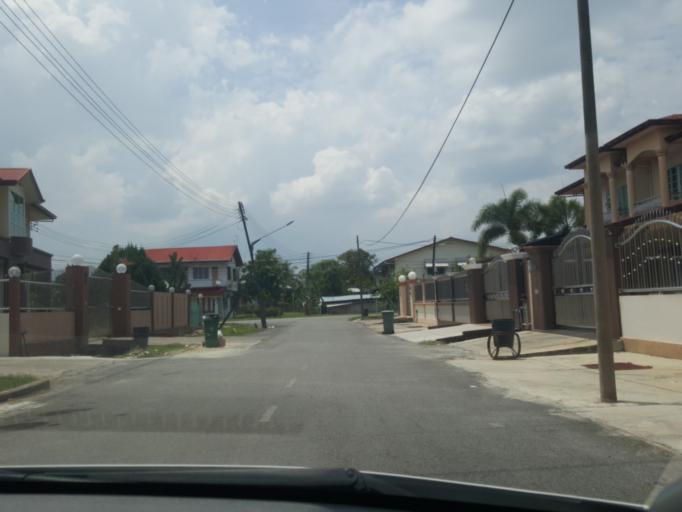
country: MY
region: Sarawak
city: Sarikei
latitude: 2.1262
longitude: 111.5234
